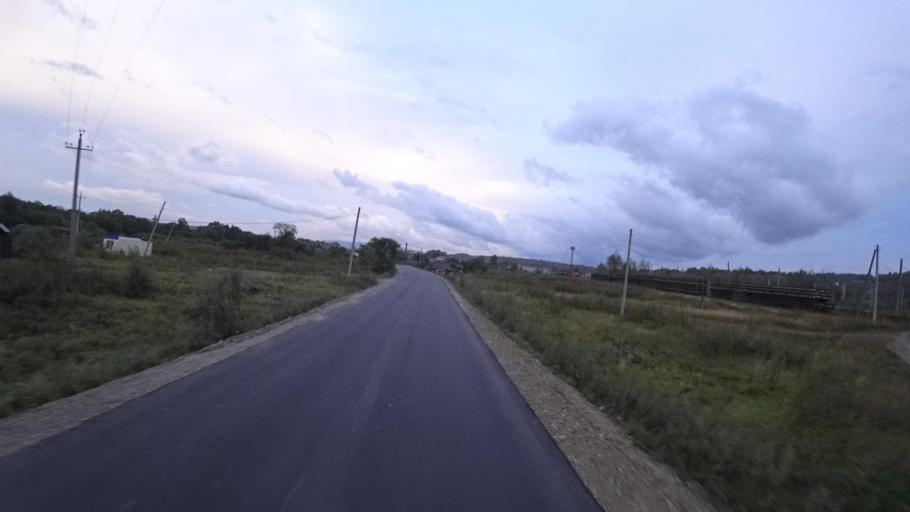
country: RU
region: Jewish Autonomous Oblast
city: Izvestkovyy
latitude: 48.9910
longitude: 131.5450
